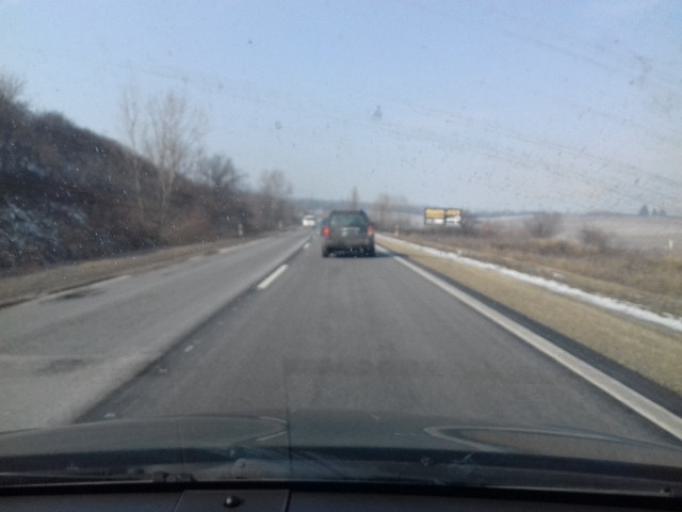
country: HU
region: Pest
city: Kosd
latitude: 47.7863
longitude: 19.1661
